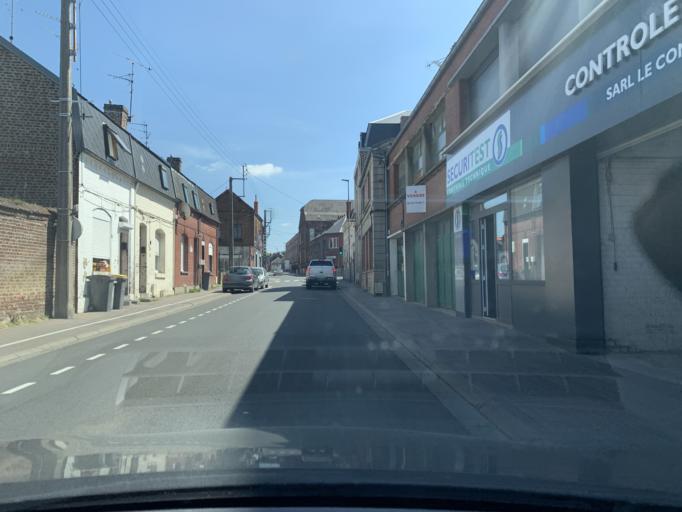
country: FR
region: Nord-Pas-de-Calais
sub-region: Departement du Nord
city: Caudry
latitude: 50.1213
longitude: 3.4024
